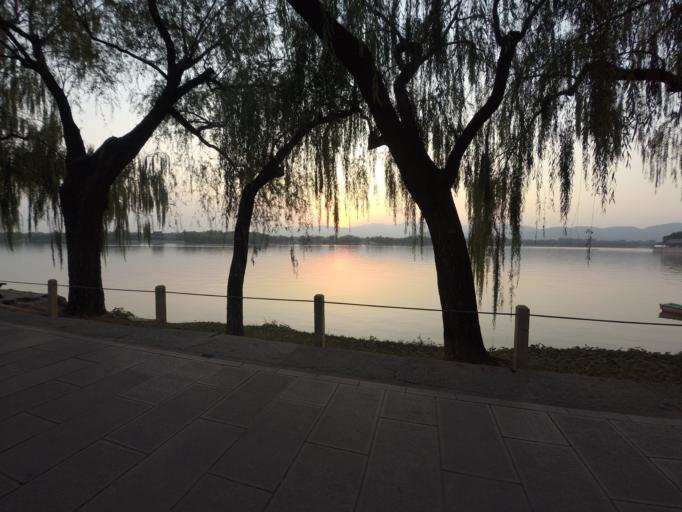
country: CN
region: Beijing
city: Haidian
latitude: 39.9877
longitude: 116.2723
